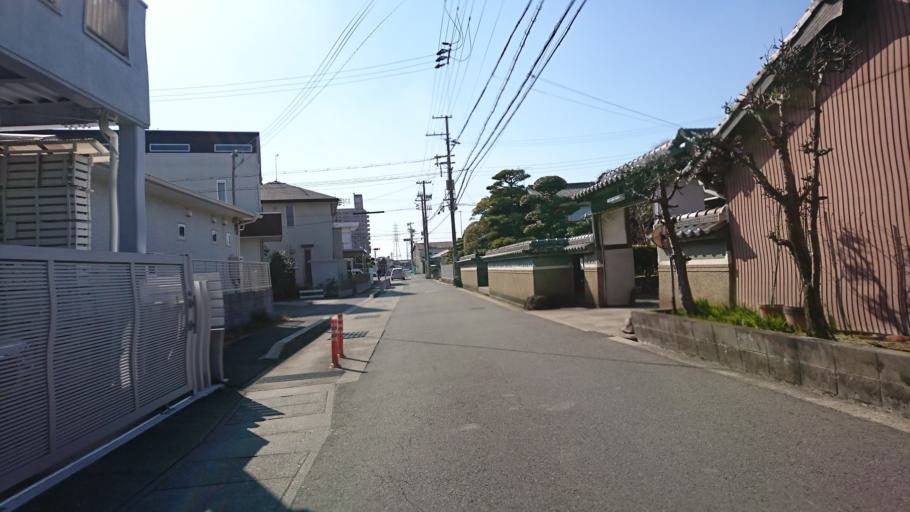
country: JP
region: Hyogo
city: Kakogawacho-honmachi
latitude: 34.7310
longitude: 134.8602
